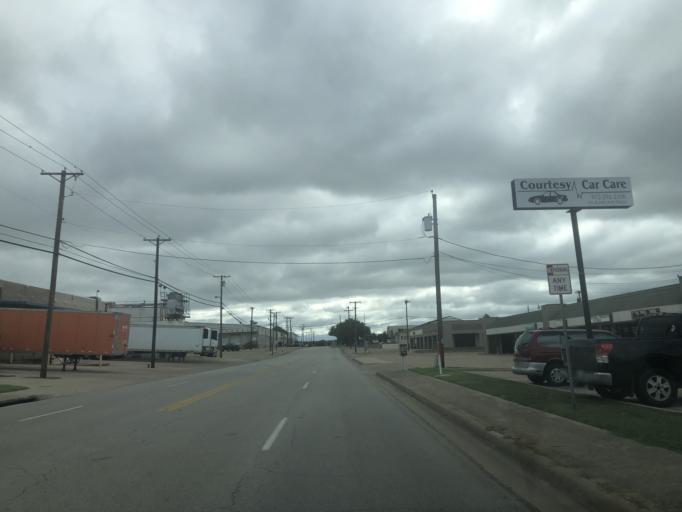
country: US
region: Texas
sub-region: Dallas County
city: Duncanville
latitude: 32.6421
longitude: -96.9240
